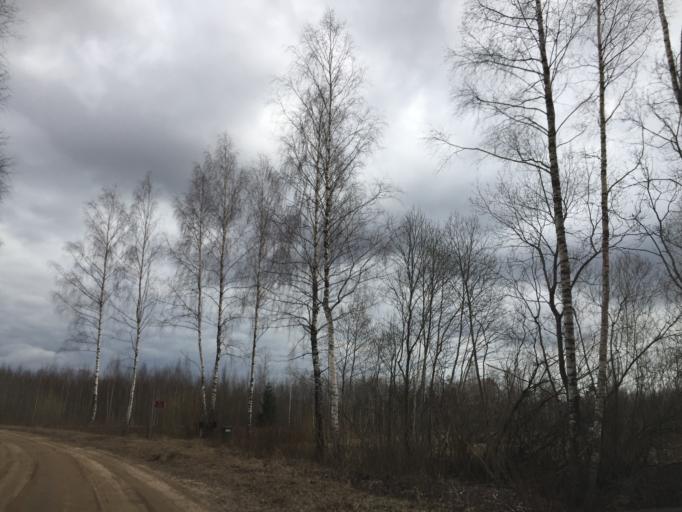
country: LV
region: Jaunjelgava
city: Jaunjelgava
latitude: 56.5947
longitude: 25.0528
